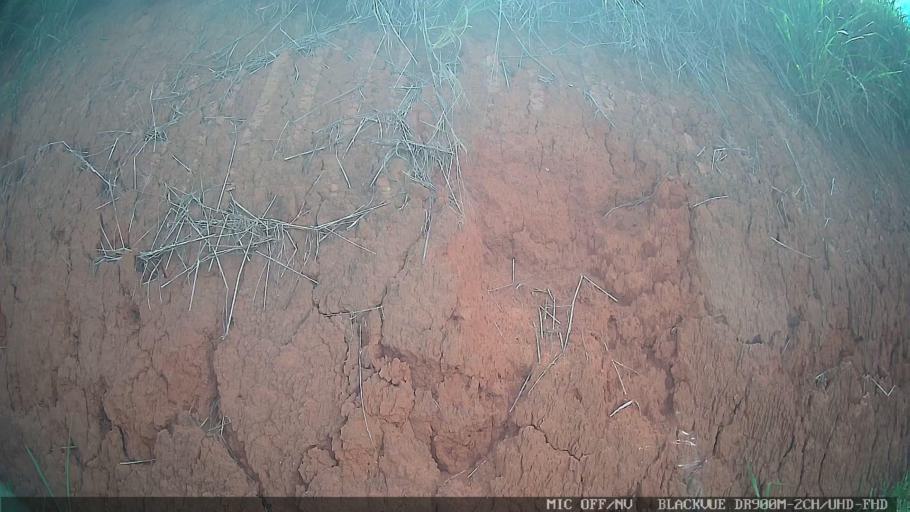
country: BR
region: Sao Paulo
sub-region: Atibaia
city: Atibaia
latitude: -23.0589
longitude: -46.5068
